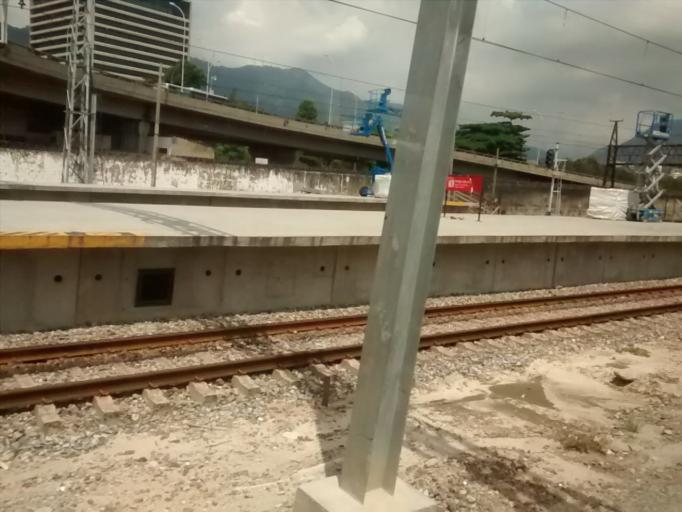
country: BR
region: Rio de Janeiro
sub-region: Rio De Janeiro
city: Rio de Janeiro
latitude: -22.9096
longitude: -43.2241
